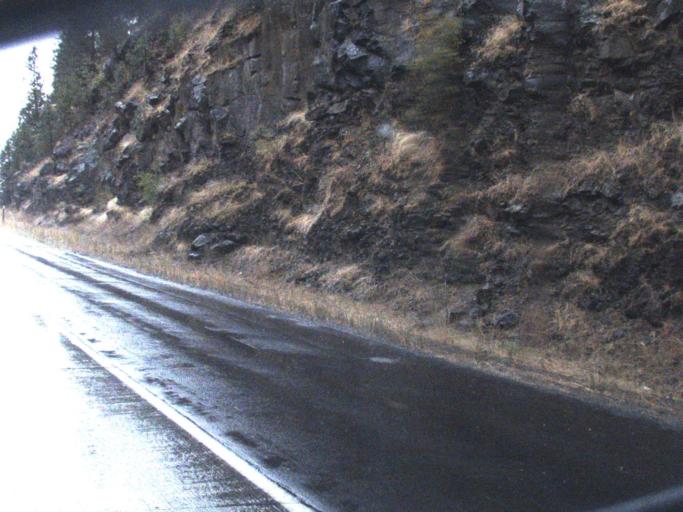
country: US
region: Washington
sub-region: Spokane County
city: Spokane
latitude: 47.5546
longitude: -117.3960
